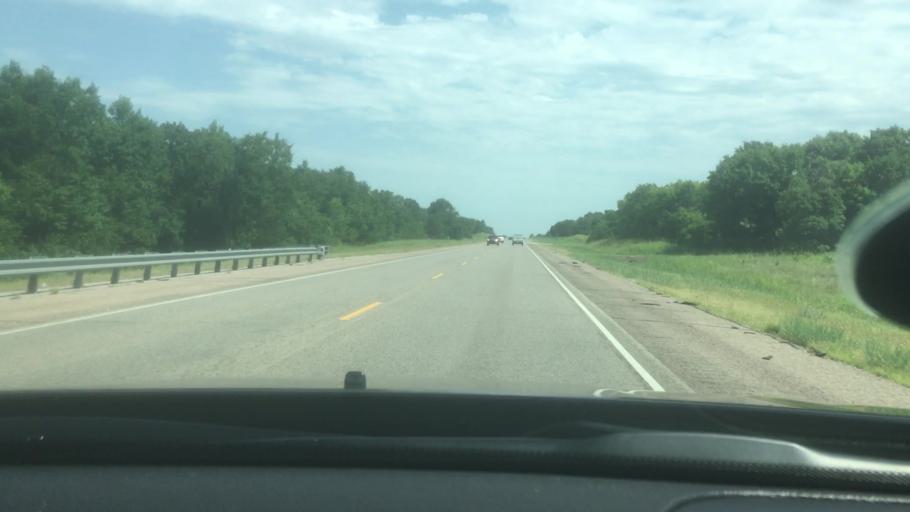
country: US
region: Oklahoma
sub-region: Seminole County
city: Konawa
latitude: 35.0122
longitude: -96.9314
